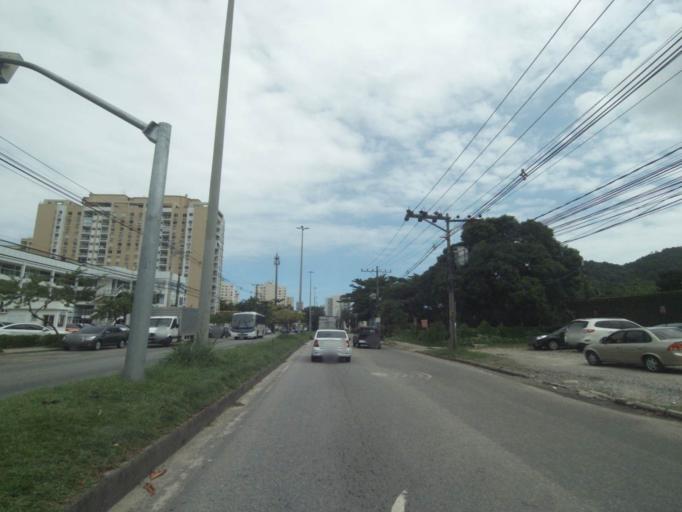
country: BR
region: Rio de Janeiro
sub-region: Nilopolis
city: Nilopolis
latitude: -22.9697
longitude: -43.4137
